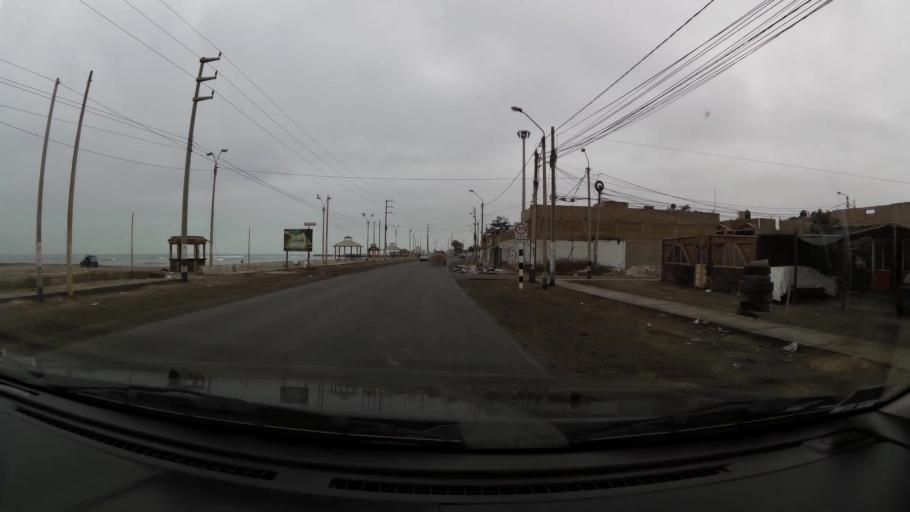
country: PE
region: Ica
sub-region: Provincia de Pisco
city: Pisco
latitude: -13.7380
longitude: -76.2258
